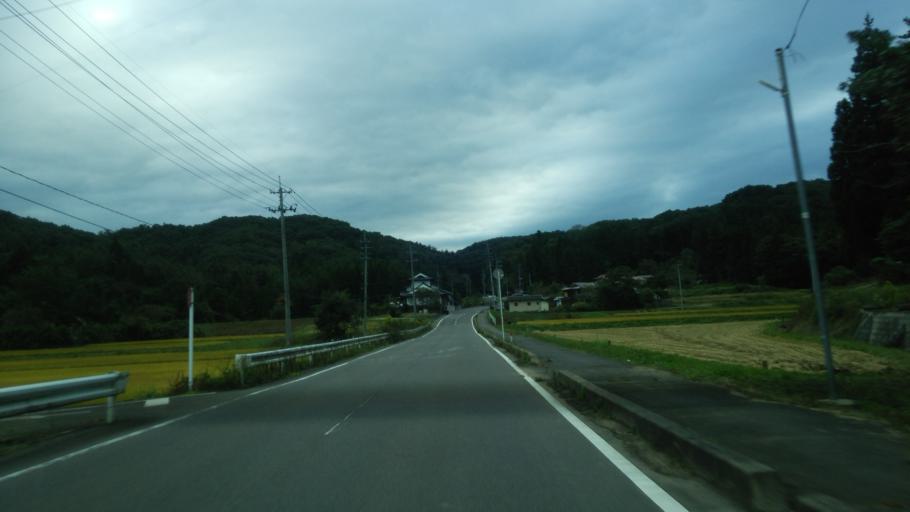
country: JP
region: Fukushima
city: Sukagawa
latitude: 37.2649
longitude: 140.2543
